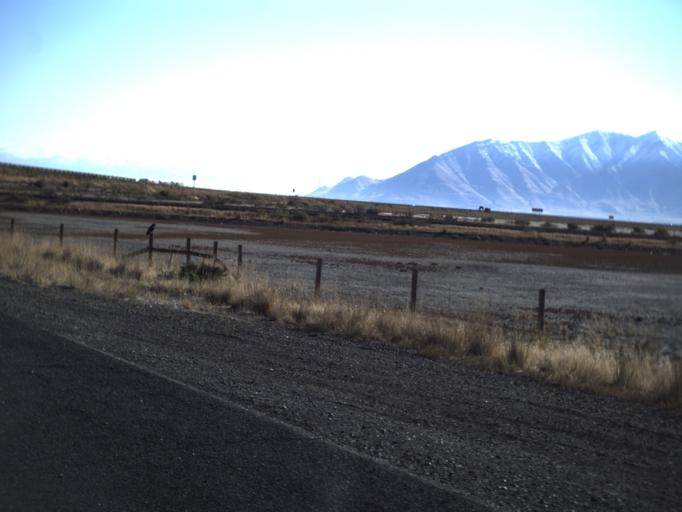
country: US
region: Utah
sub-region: Tooele County
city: Grantsville
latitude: 40.6818
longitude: -112.4408
